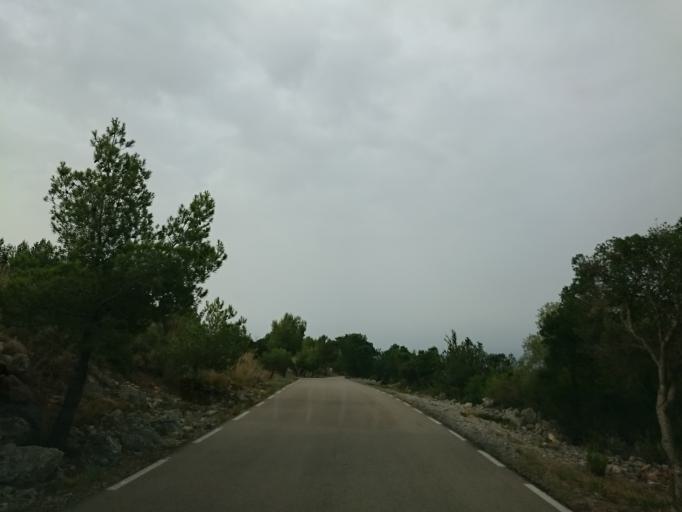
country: ES
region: Catalonia
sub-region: Provincia de Barcelona
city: Castelldefels
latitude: 41.2768
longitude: 1.9138
